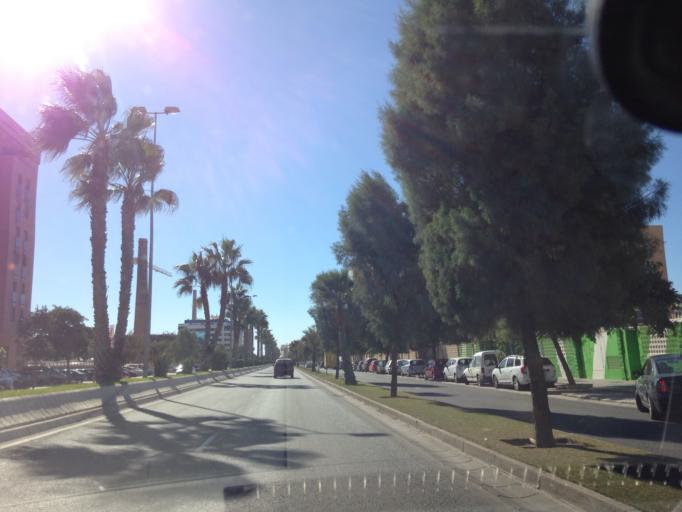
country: ES
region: Andalusia
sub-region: Provincia de Malaga
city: Malaga
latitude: 36.6993
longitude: -4.4368
